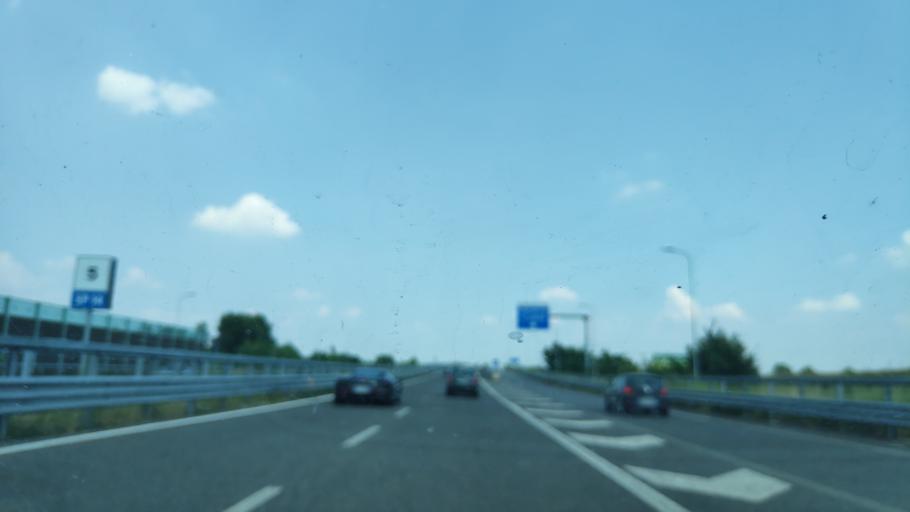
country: IT
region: Lombardy
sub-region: Citta metropolitana di Milano
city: Millepini
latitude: 45.4795
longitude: 9.3278
